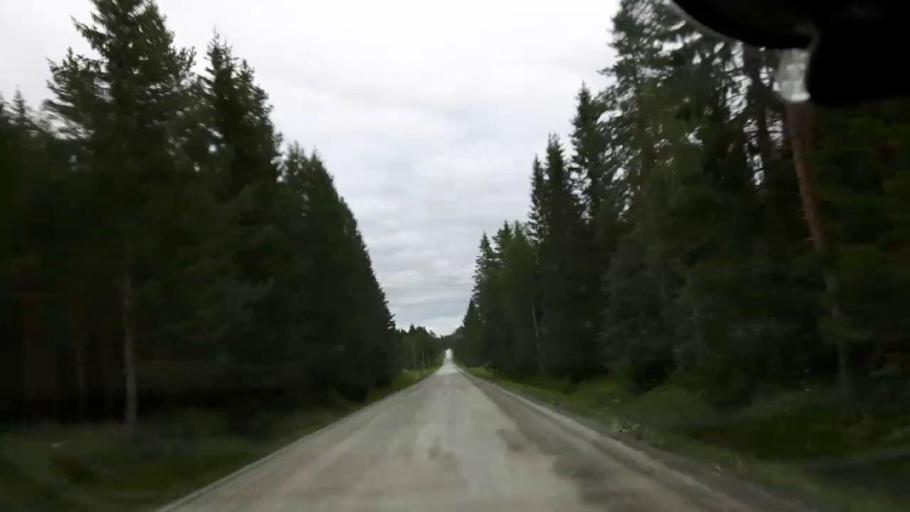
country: SE
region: Jaemtland
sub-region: OEstersunds Kommun
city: Brunflo
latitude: 63.0991
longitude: 15.1182
